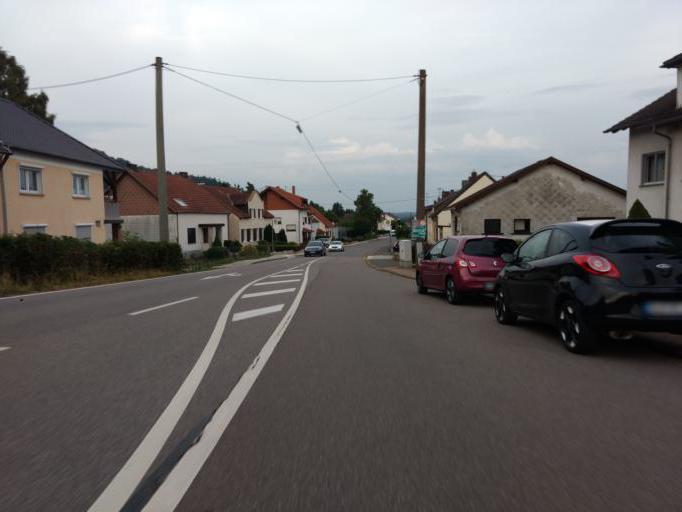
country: DE
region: Saarland
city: Wallerfangen
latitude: 49.3303
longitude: 6.6976
